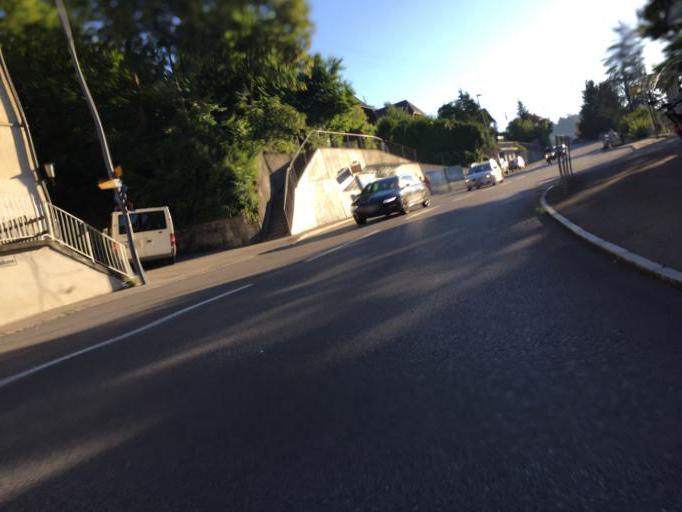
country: CH
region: Bern
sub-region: Bern-Mittelland District
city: Kirchlindach
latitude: 46.9729
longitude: 7.4178
